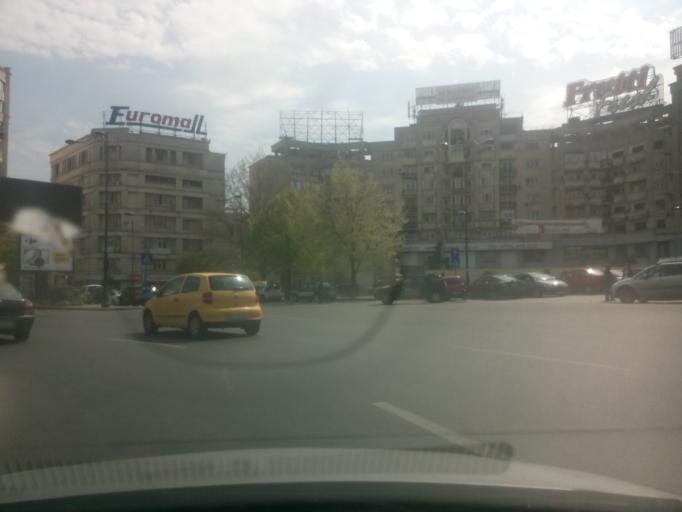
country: RO
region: Bucuresti
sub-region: Municipiul Bucuresti
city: Bucuresti
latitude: 44.4263
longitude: 26.1010
